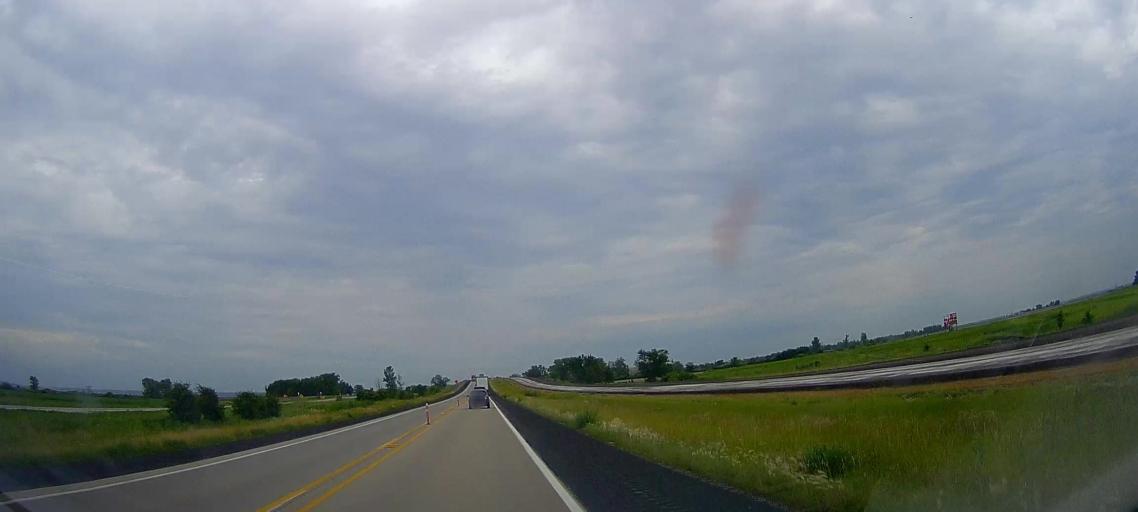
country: US
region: Nebraska
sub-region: Washington County
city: Blair
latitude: 41.6438
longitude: -96.0180
